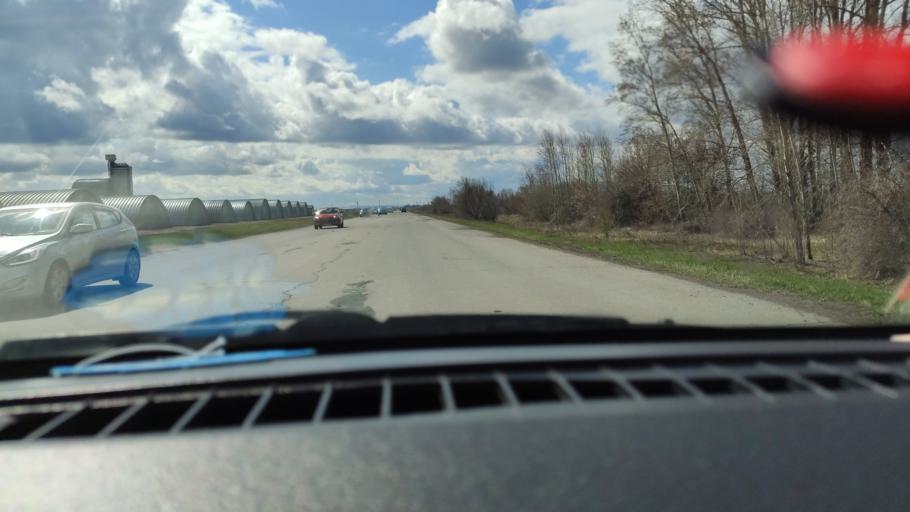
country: RU
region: Samara
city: Tol'yatti
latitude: 53.6849
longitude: 49.4168
